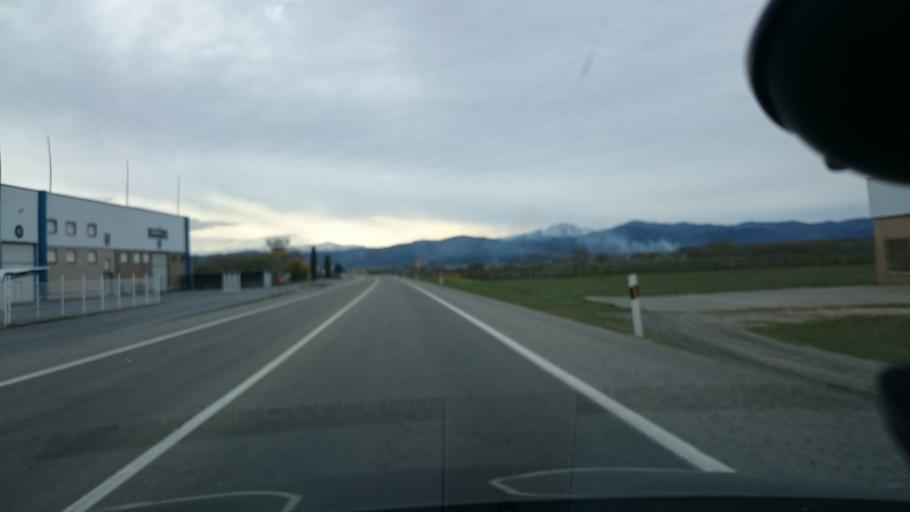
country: ES
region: Castille and Leon
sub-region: Provincia de Leon
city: Carracedelo
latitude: 42.5651
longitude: -6.7062
